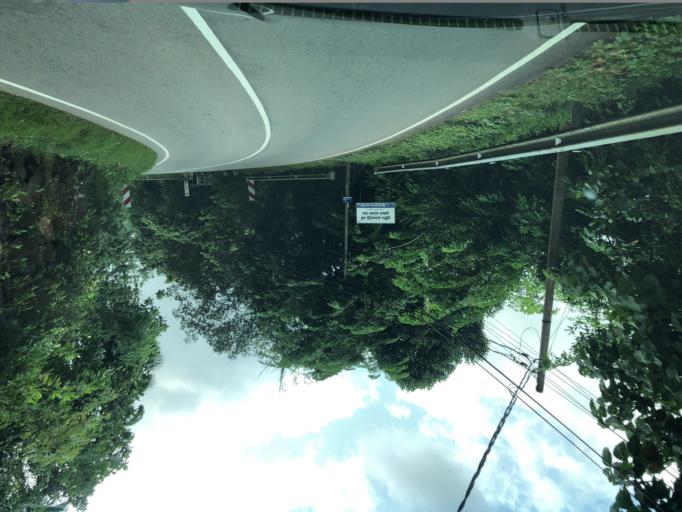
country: LK
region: Western
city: Horana South
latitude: 6.6815
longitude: 80.1312
